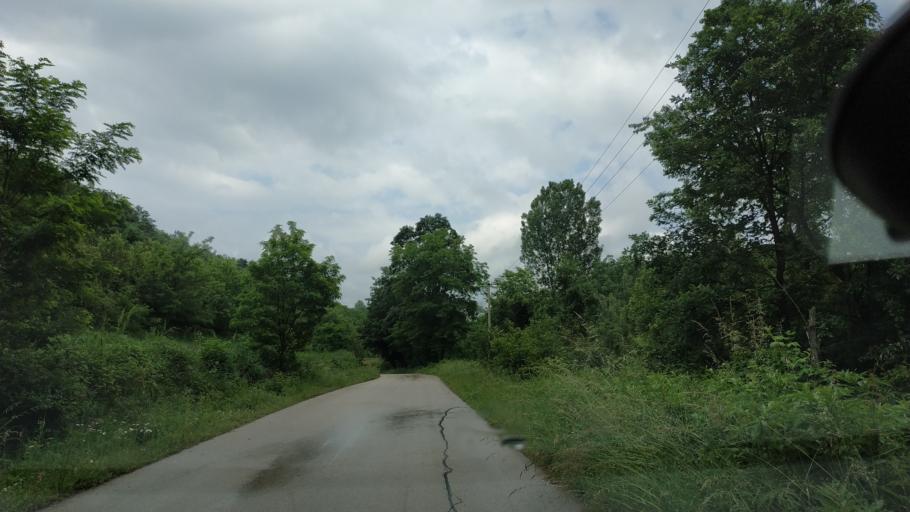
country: RS
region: Central Serbia
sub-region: Nisavski Okrug
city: Aleksinac
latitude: 43.4207
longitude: 21.5677
